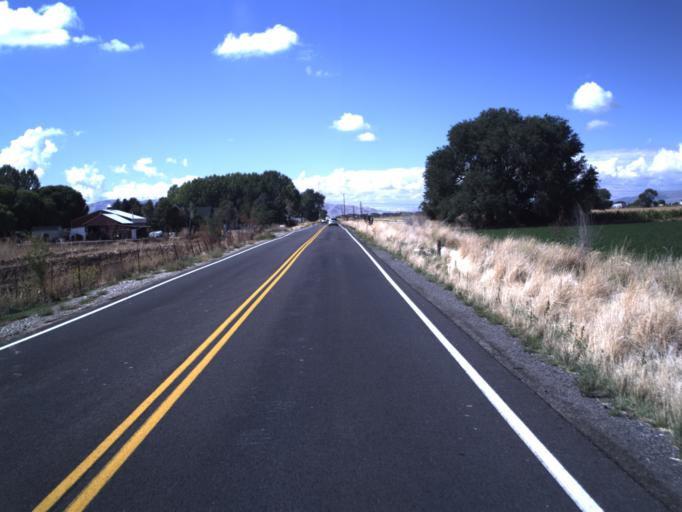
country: US
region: Utah
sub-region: Utah County
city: Mapleton
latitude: 40.1156
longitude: -111.6010
